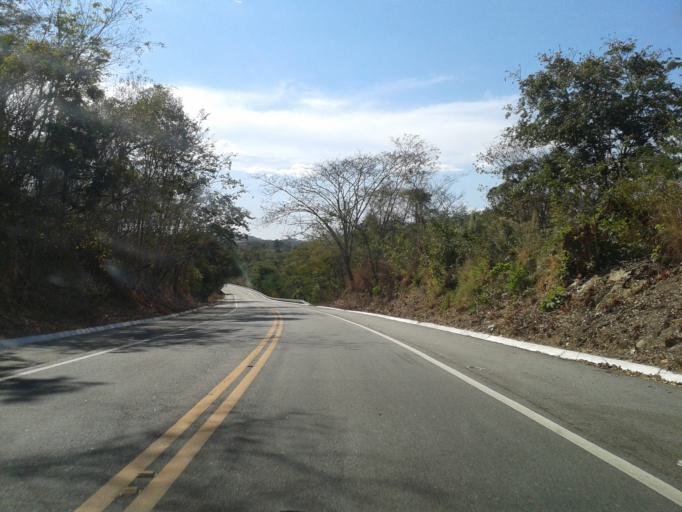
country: BR
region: Goias
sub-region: Goias
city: Goias
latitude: -15.8091
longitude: -50.1196
